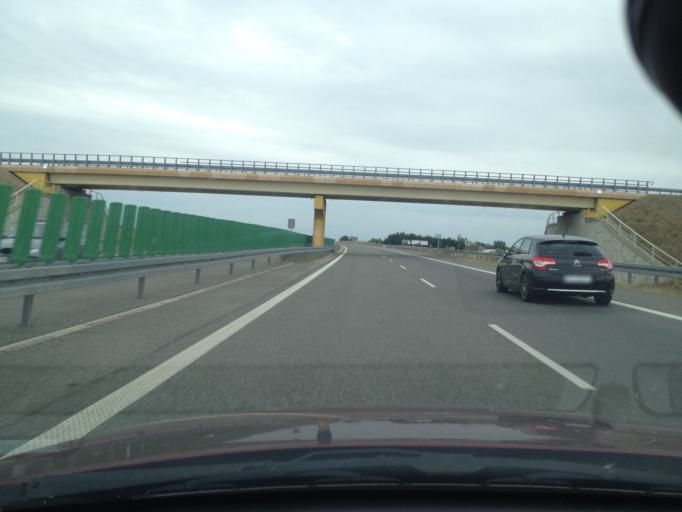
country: PL
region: Lubusz
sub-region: Powiat gorzowski
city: Jenin
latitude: 52.7634
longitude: 15.1333
